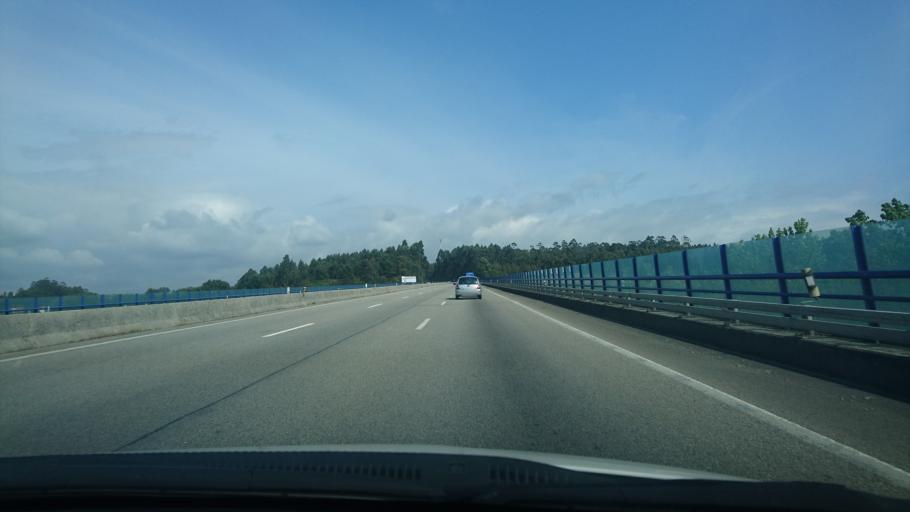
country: PT
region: Porto
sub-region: Vila Nova de Gaia
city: Grijo
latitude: 41.0112
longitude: -8.5702
